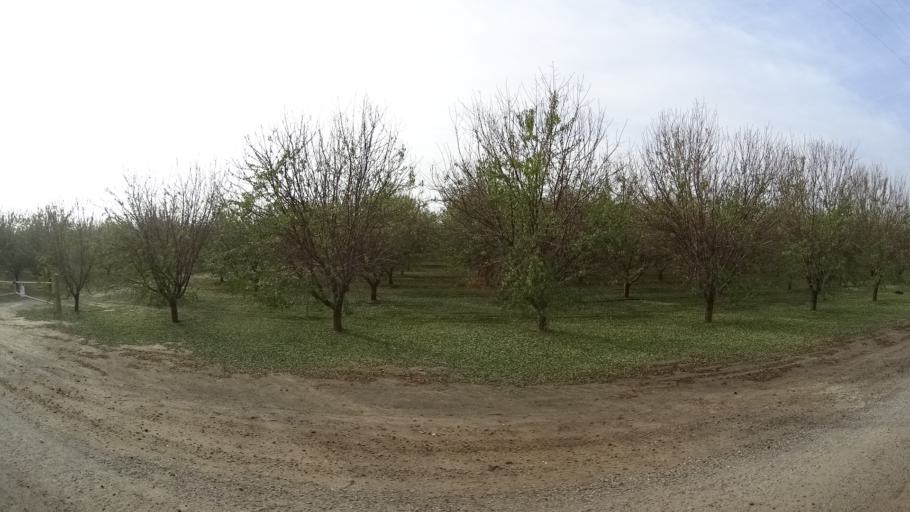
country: US
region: California
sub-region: Kern County
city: Greenacres
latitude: 35.2856
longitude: -119.1283
